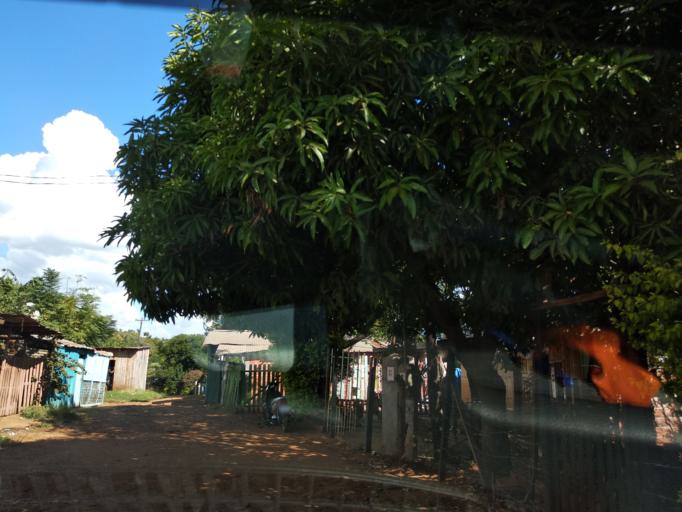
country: AR
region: Misiones
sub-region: Departamento de Capital
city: Posadas
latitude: -27.3909
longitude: -55.9466
